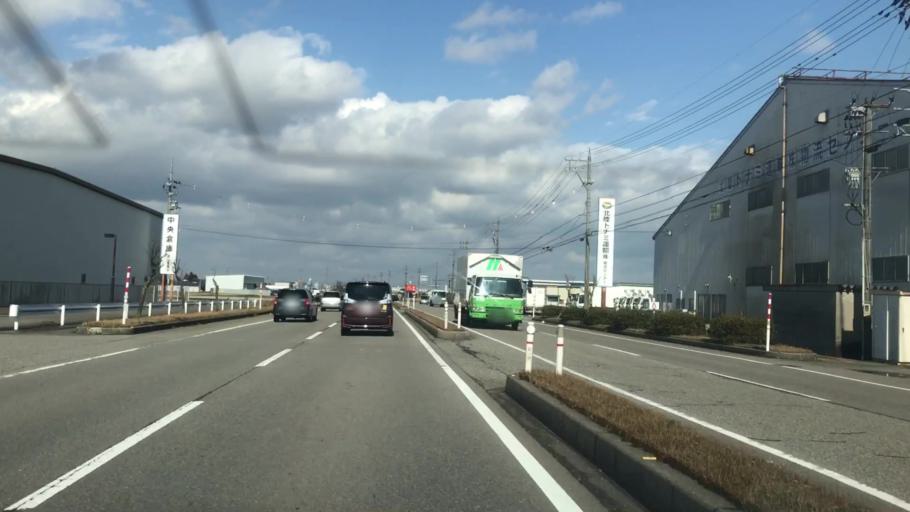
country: JP
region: Toyama
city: Kuragaki-kosugi
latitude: 36.7090
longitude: 137.0800
